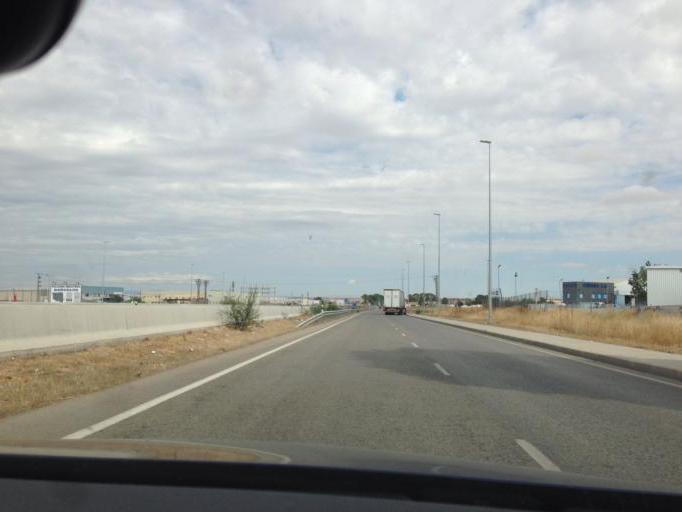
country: ES
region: Madrid
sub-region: Provincia de Madrid
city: Alcala de Henares
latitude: 40.5065
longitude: -3.4003
